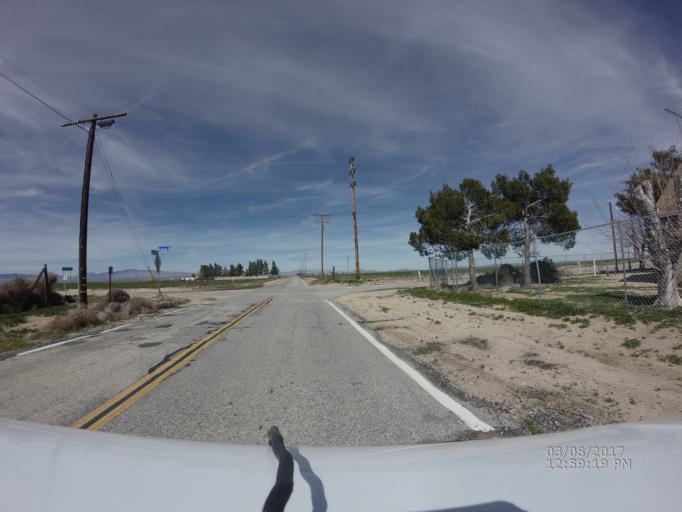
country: US
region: California
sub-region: Los Angeles County
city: Quartz Hill
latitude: 34.7184
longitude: -118.2545
